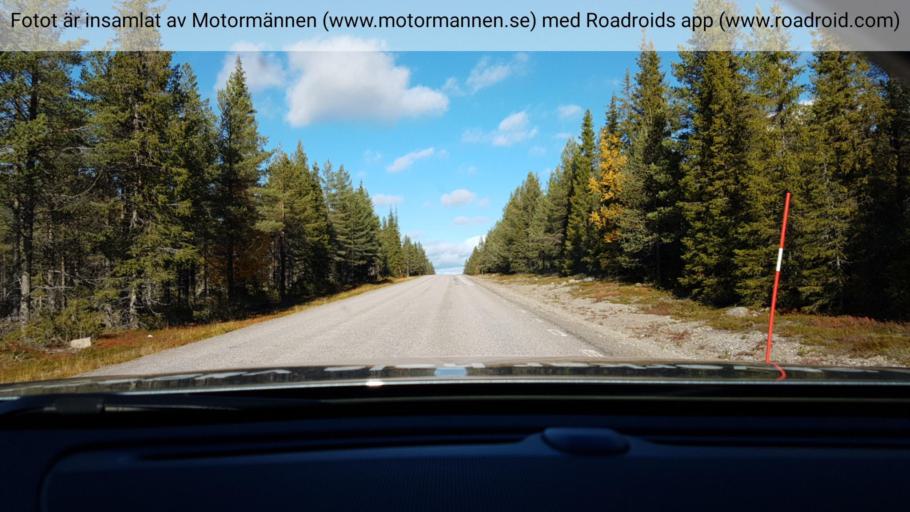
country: SE
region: Norrbotten
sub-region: Arjeplogs Kommun
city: Arjeplog
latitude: 65.8301
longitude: 18.4332
